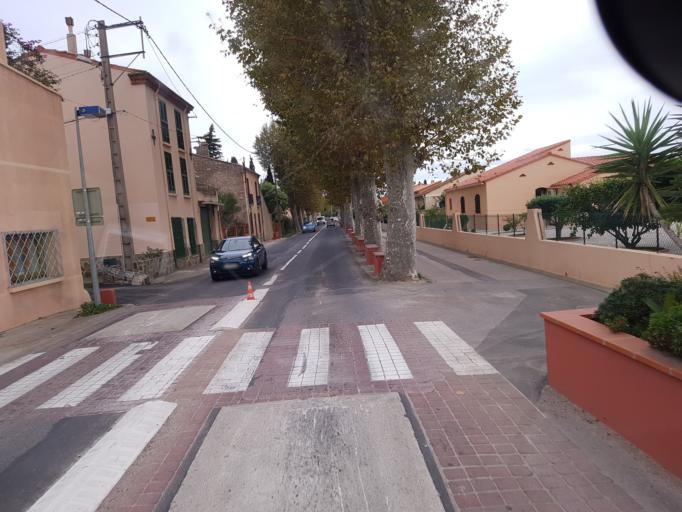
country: FR
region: Languedoc-Roussillon
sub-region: Departement des Pyrenees-Orientales
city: Torreilles
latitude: 42.7612
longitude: 2.9890
